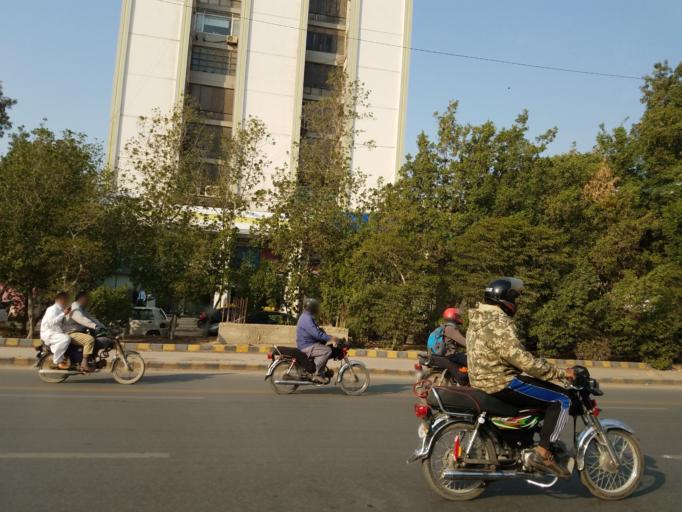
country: PK
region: Sindh
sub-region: Karachi District
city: Karachi
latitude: 24.8598
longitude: 67.0564
